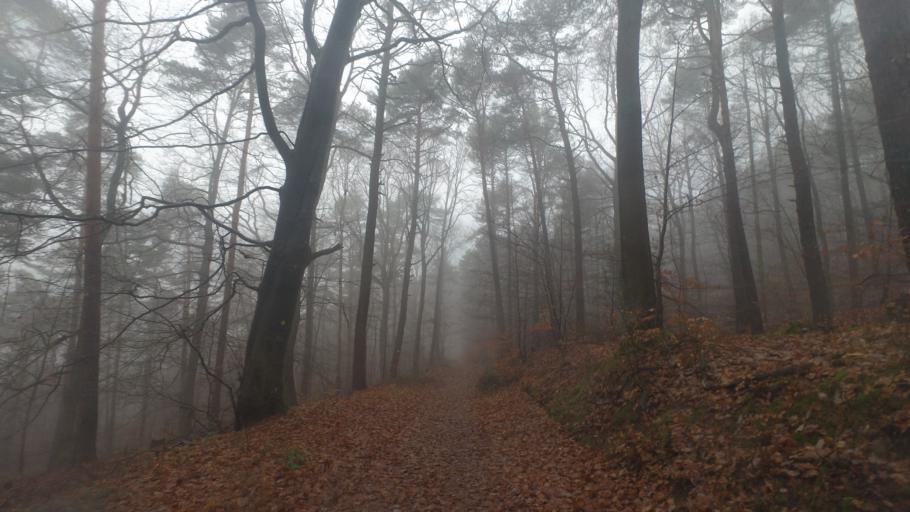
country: DE
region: Rheinland-Pfalz
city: Altleiningen
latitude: 49.4844
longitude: 8.0963
